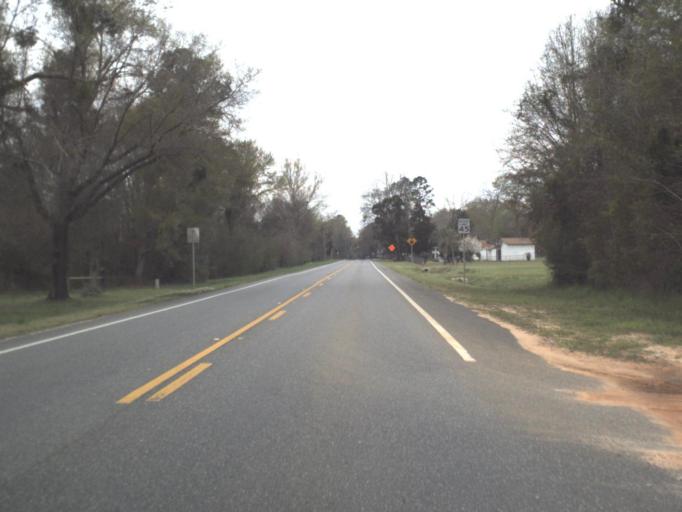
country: US
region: Florida
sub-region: Calhoun County
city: Blountstown
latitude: 30.4403
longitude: -85.1838
